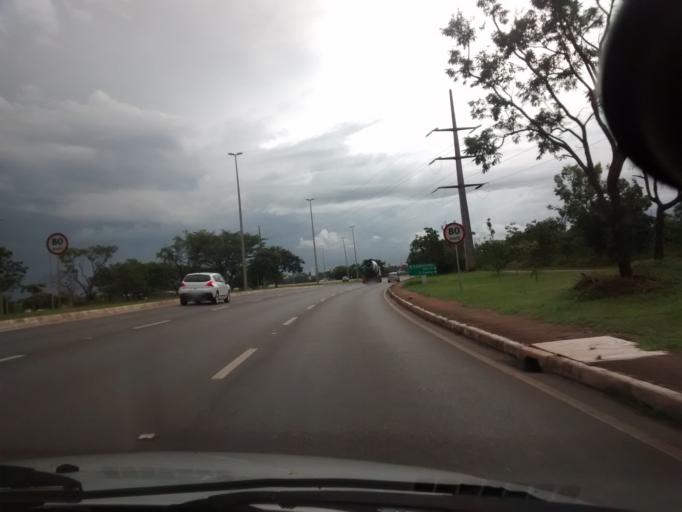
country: BR
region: Federal District
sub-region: Brasilia
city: Brasilia
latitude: -15.7724
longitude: -47.8640
